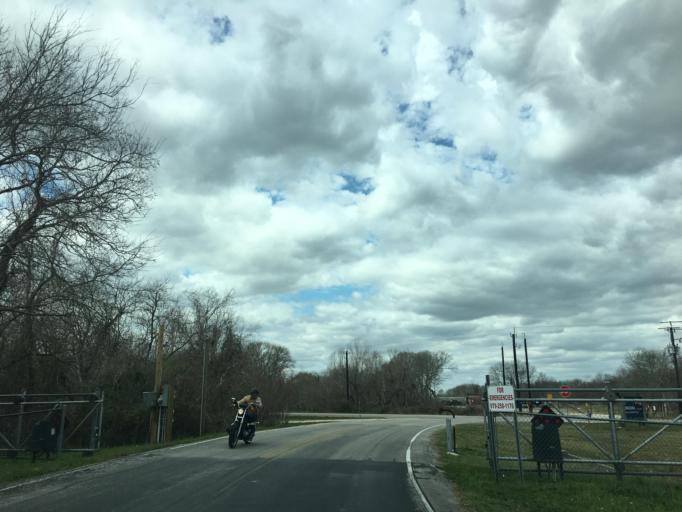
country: US
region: Texas
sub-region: Brazoria County
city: Oyster Creek
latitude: 29.0650
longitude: -95.3187
